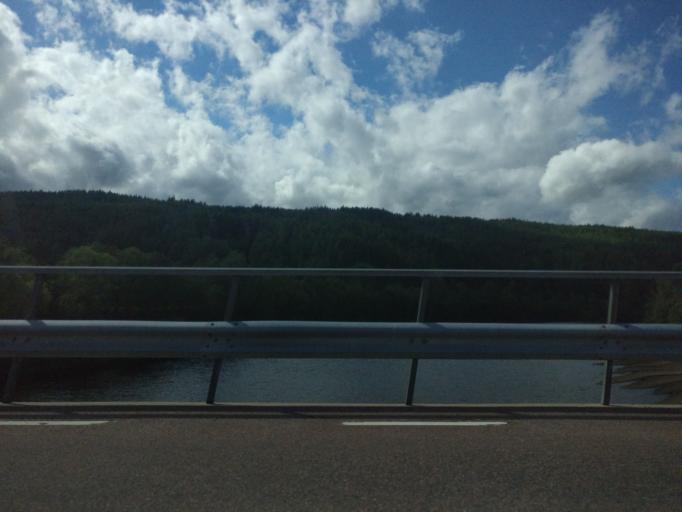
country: SE
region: Vaermland
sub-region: Hagfors Kommun
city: Ekshaerad
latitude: 60.2893
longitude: 13.3945
